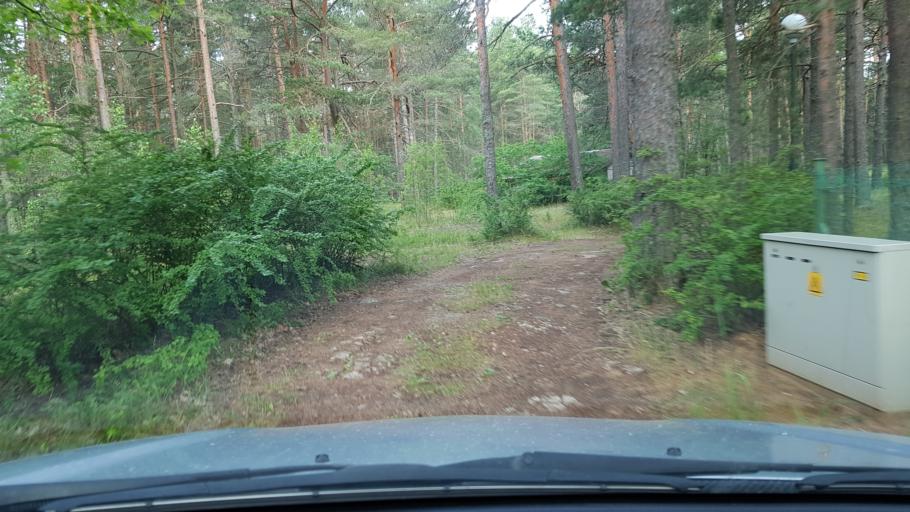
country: EE
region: Ida-Virumaa
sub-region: Narva-Joesuu linn
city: Narva-Joesuu
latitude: 59.4515
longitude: 28.0516
